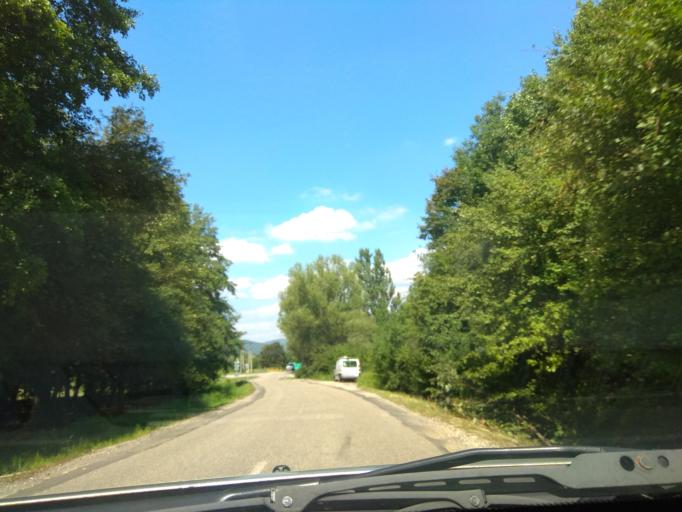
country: HU
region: Borsod-Abauj-Zemplen
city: Harsany
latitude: 47.9975
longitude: 20.7601
